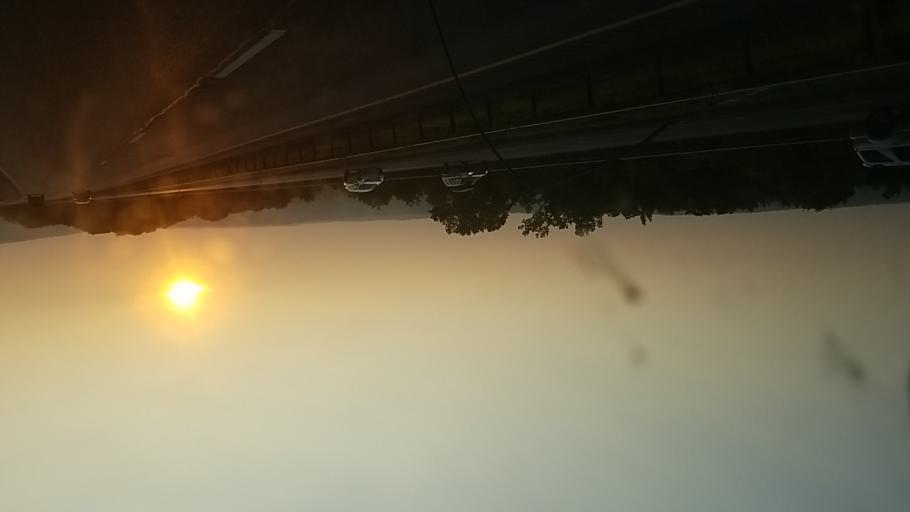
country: US
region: New York
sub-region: Herkimer County
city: Ilion
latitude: 43.0272
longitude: -75.0340
